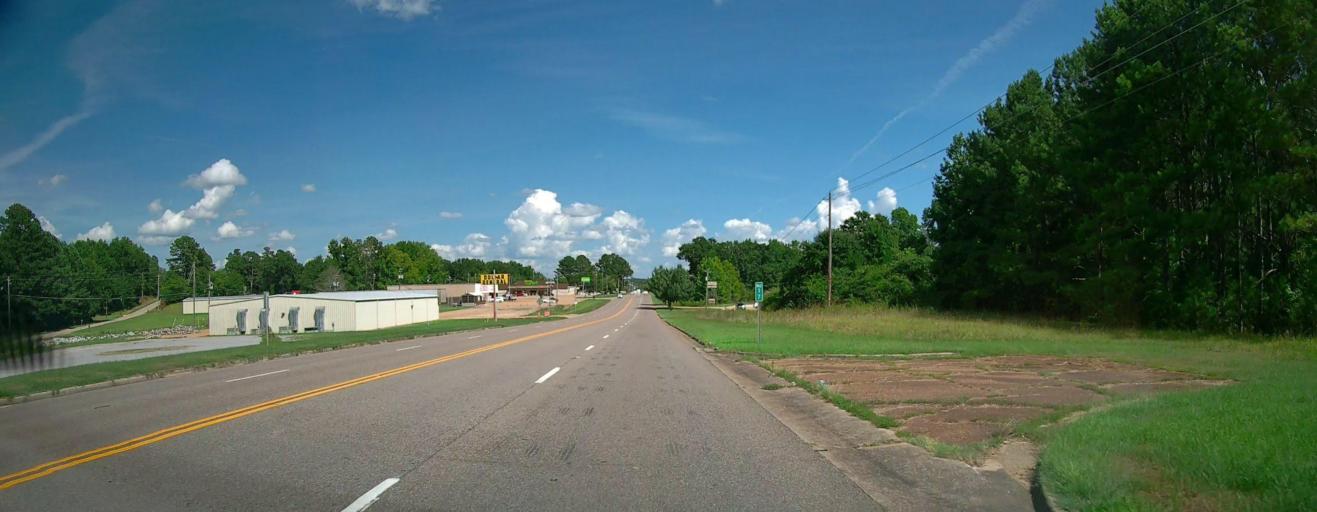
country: US
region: Alabama
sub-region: Pickens County
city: Reform
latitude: 33.3845
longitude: -88.0274
